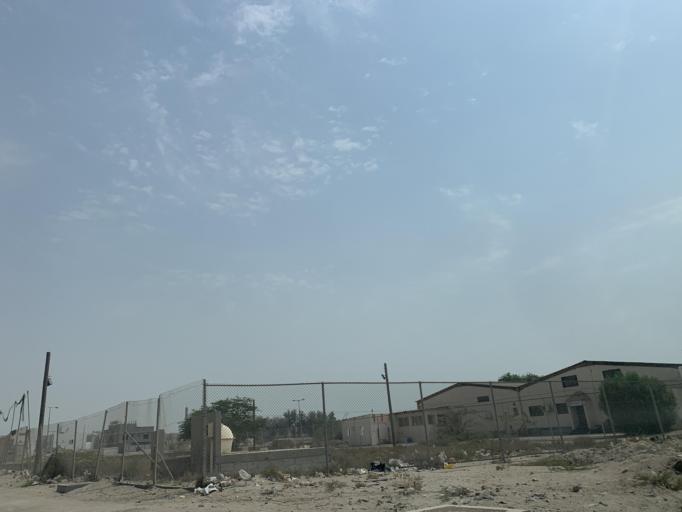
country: BH
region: Manama
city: Jidd Hafs
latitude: 26.2167
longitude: 50.4844
